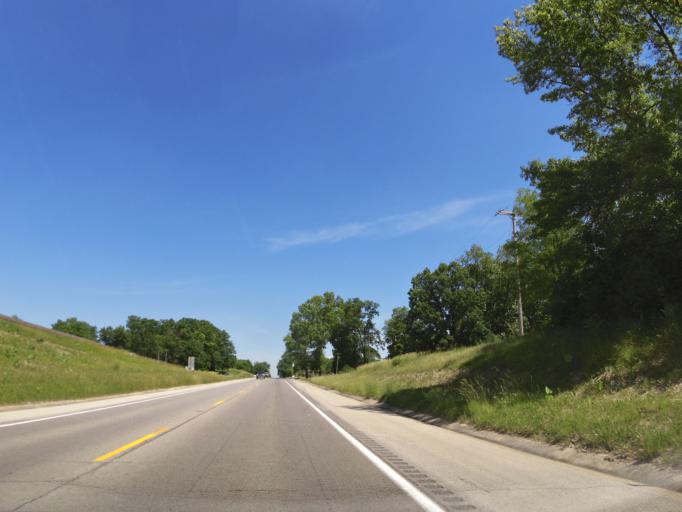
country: US
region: Illinois
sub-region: Vermilion County
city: Danville
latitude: 40.2195
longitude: -87.6396
